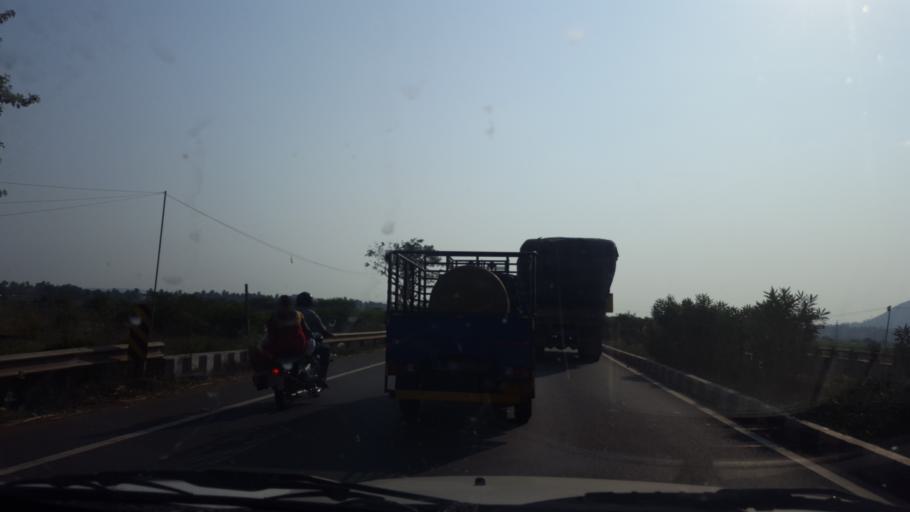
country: IN
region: Andhra Pradesh
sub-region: Vishakhapatnam
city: Etikoppaka
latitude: 17.4417
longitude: 82.7531
